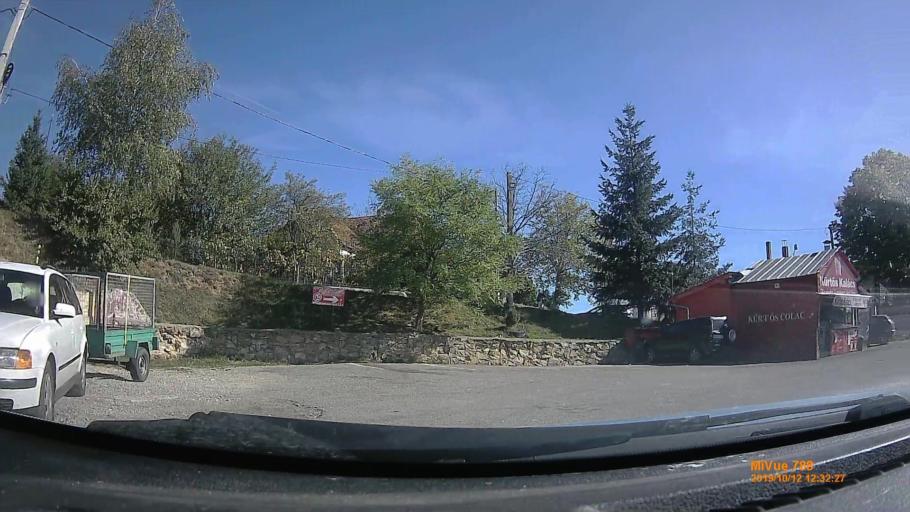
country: RO
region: Bihor
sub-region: Comuna Borod
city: Borod
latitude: 46.9701
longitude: 22.6737
